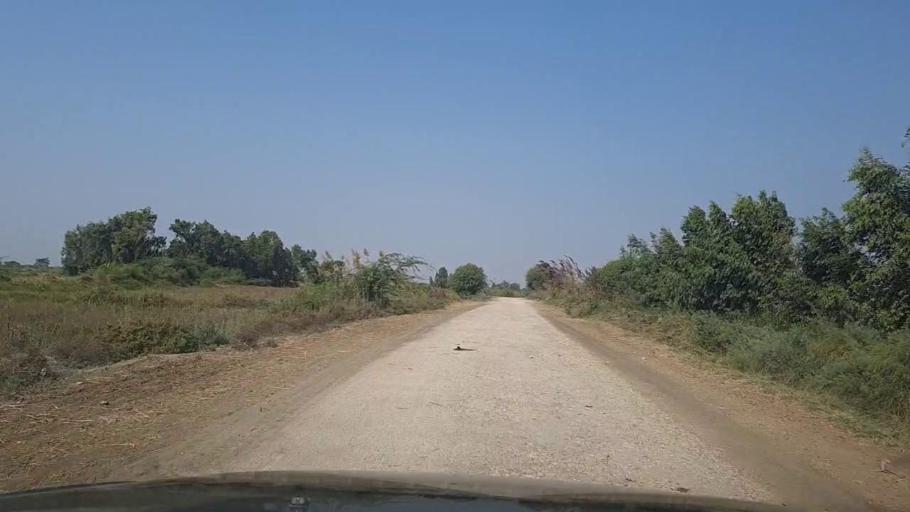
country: PK
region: Sindh
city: Thatta
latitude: 24.6188
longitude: 67.8165
